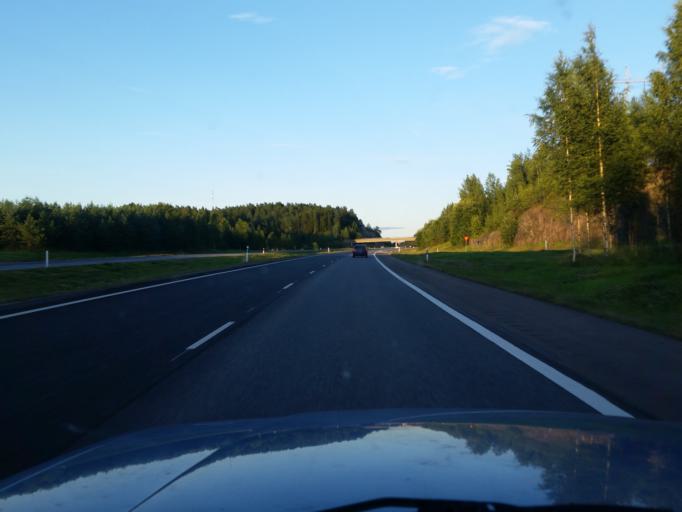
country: FI
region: Varsinais-Suomi
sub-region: Turku
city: Piikkioe
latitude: 60.4450
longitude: 22.5642
